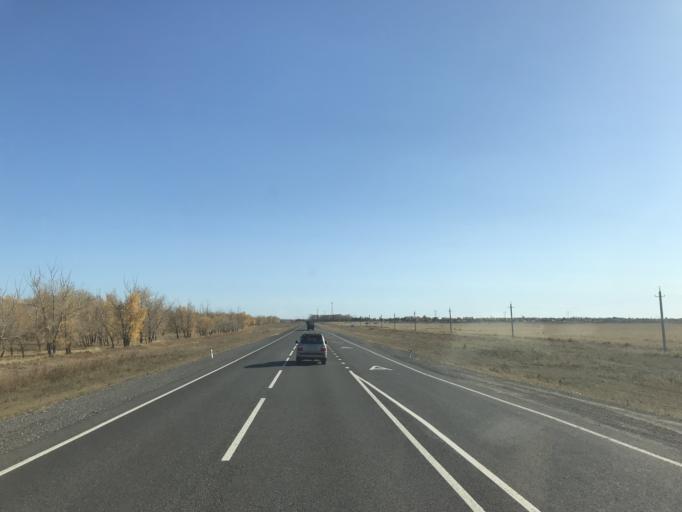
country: KZ
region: Pavlodar
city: Aksu
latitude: 51.9394
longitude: 77.3206
